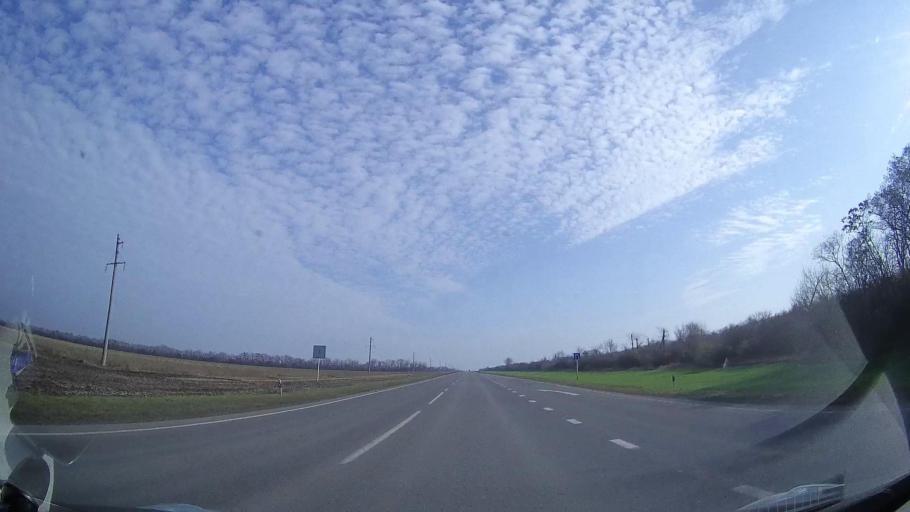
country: RU
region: Rostov
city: Gigant
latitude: 46.5257
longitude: 41.2354
